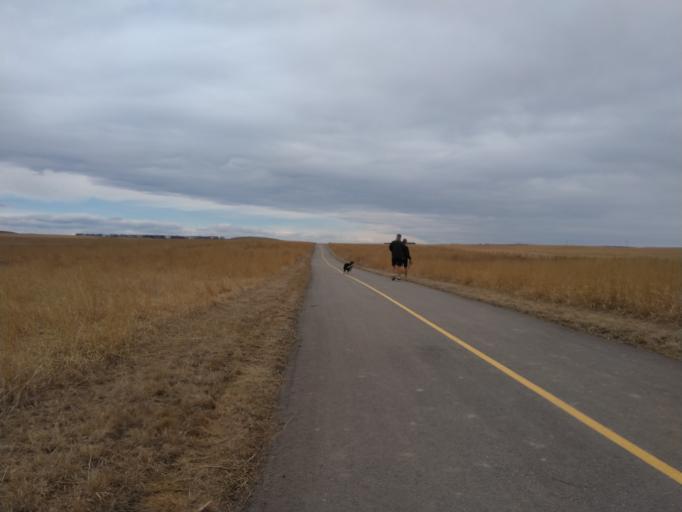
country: CA
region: Alberta
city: Airdrie
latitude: 51.1776
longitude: -114.0300
